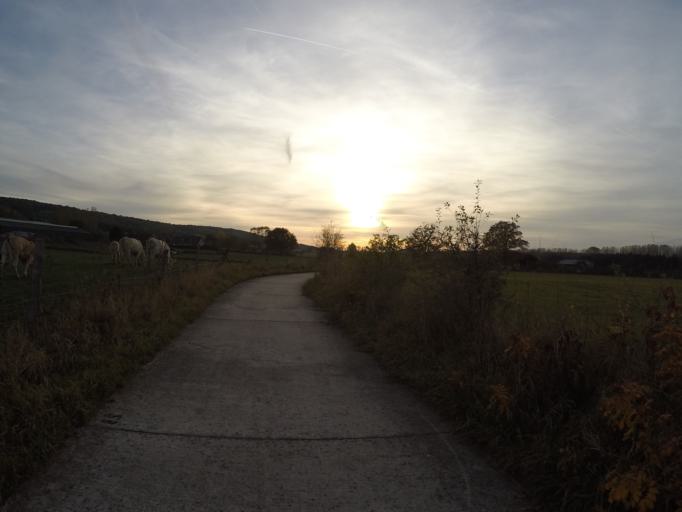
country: BE
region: Wallonia
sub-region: Province du Luxembourg
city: Hotton
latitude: 50.2498
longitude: 5.3952
